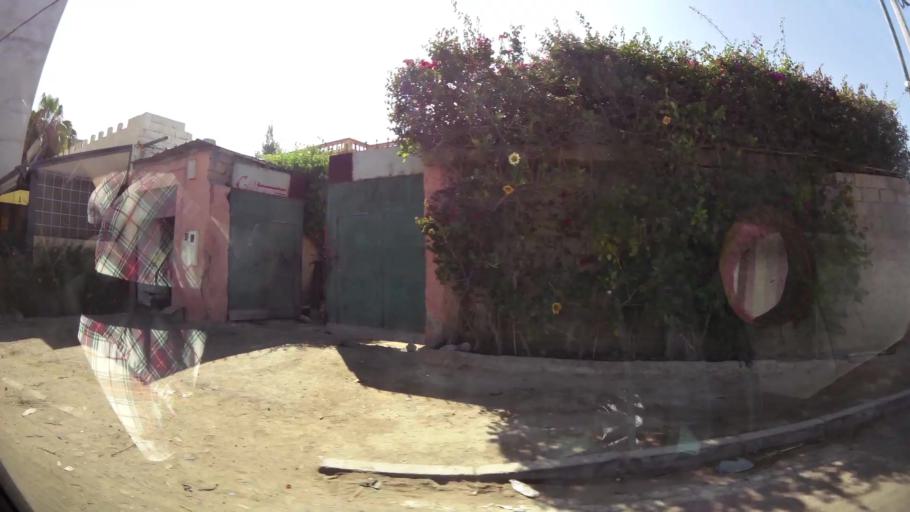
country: MA
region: Souss-Massa-Draa
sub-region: Inezgane-Ait Mellou
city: Inezgane
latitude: 30.3452
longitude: -9.5093
